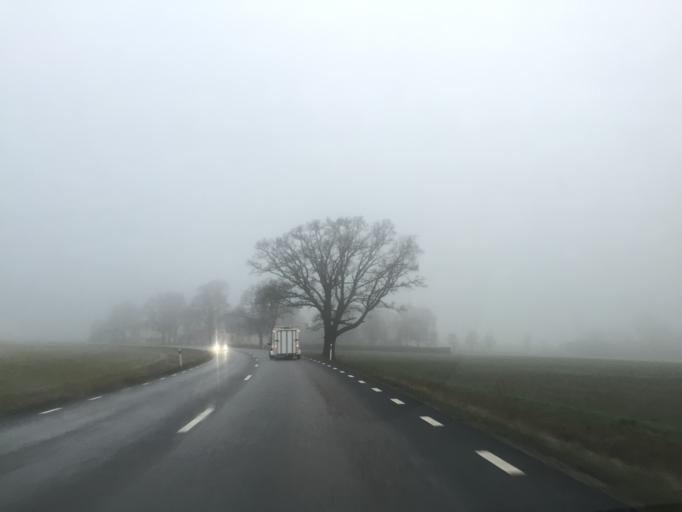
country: SE
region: Soedermanland
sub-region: Katrineholms Kommun
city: Katrineholm
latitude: 58.9663
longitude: 16.3648
